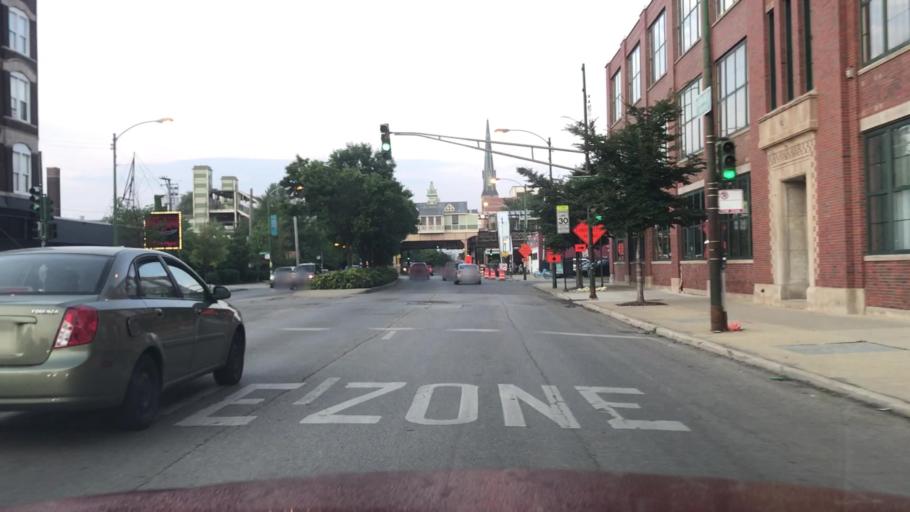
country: US
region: Illinois
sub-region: Cook County
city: Chicago
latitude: 41.8867
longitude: -87.6671
